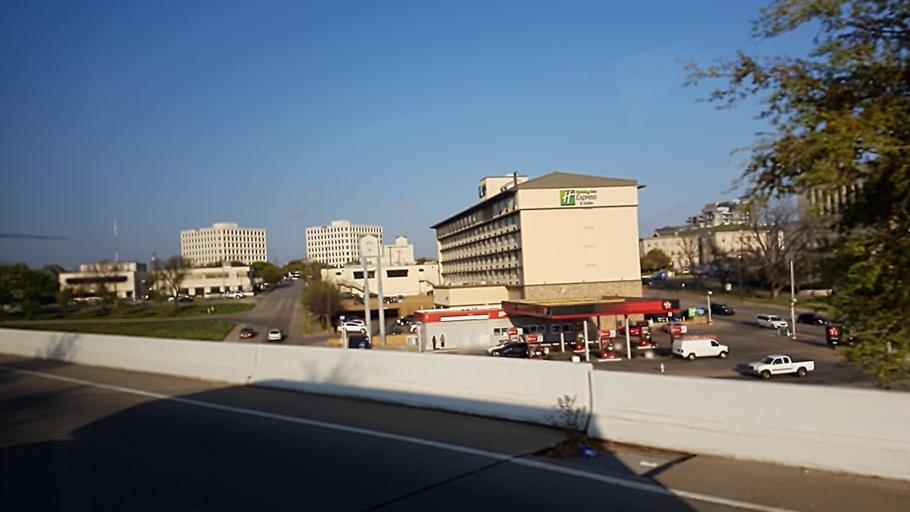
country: US
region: Texas
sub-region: Tarrant County
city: Fort Worth
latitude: 32.7462
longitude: -97.3369
